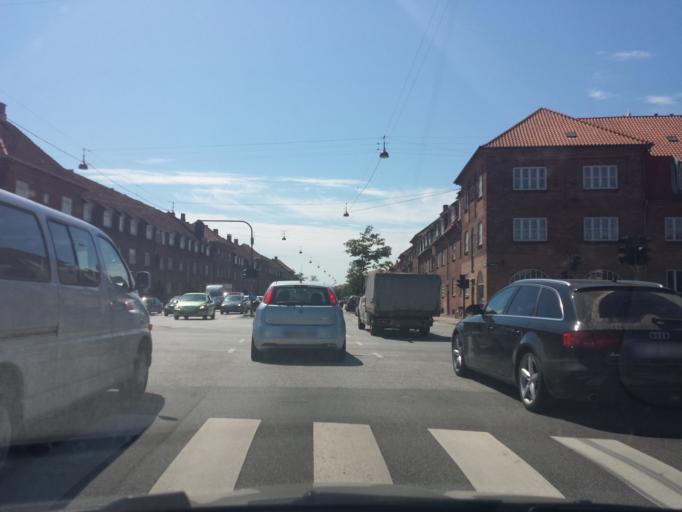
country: DK
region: Capital Region
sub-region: Frederiksberg Kommune
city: Frederiksberg
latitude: 55.6535
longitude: 12.5391
